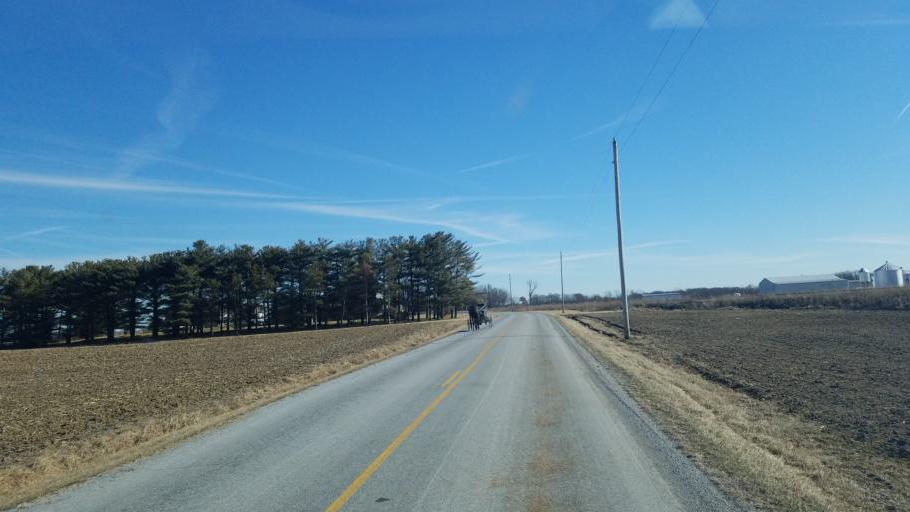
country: US
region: Ohio
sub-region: Union County
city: Richwood
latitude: 40.5648
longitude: -83.4252
